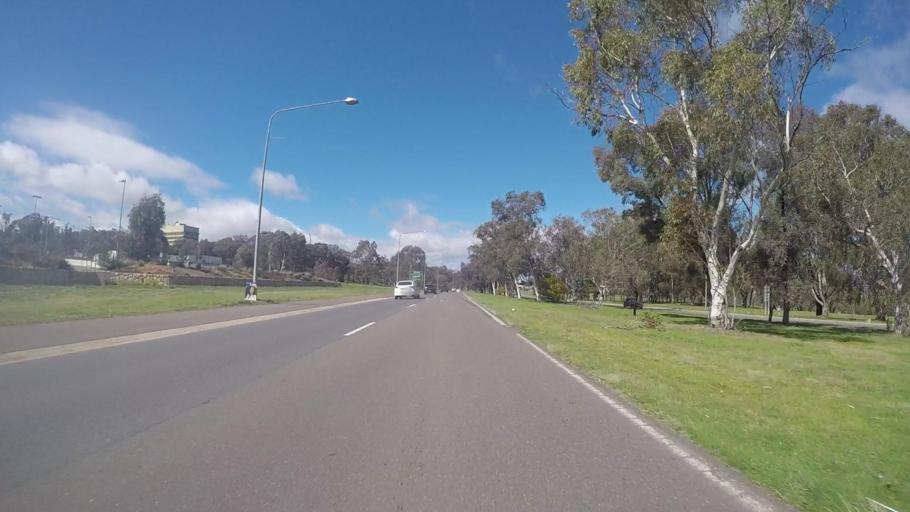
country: AU
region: Australian Capital Territory
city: Canberra
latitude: -35.2940
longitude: 149.1444
